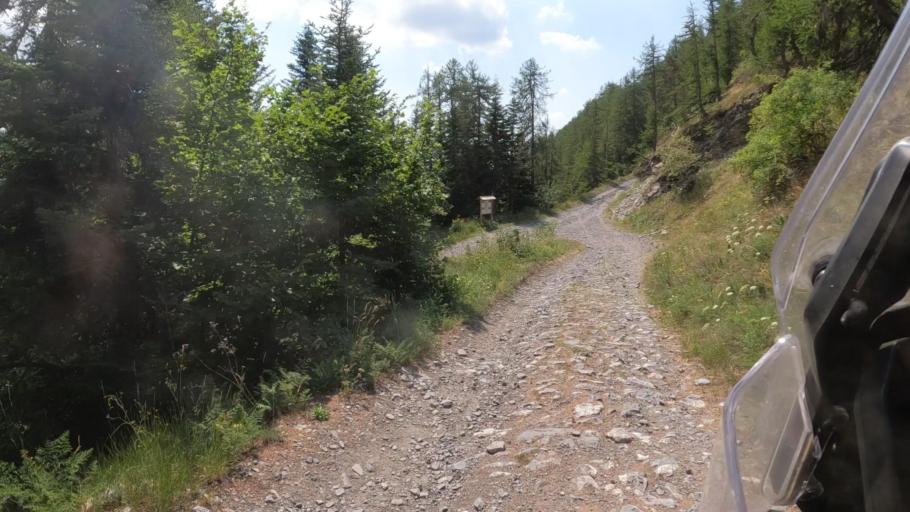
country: IT
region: Piedmont
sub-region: Provincia di Cuneo
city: Briga Alta
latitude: 44.0461
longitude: 7.7032
